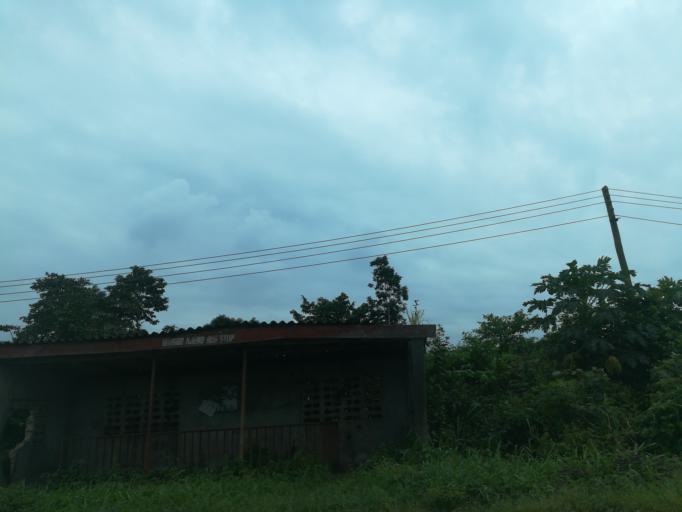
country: NG
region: Lagos
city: Ejirin
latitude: 6.6463
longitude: 3.7717
